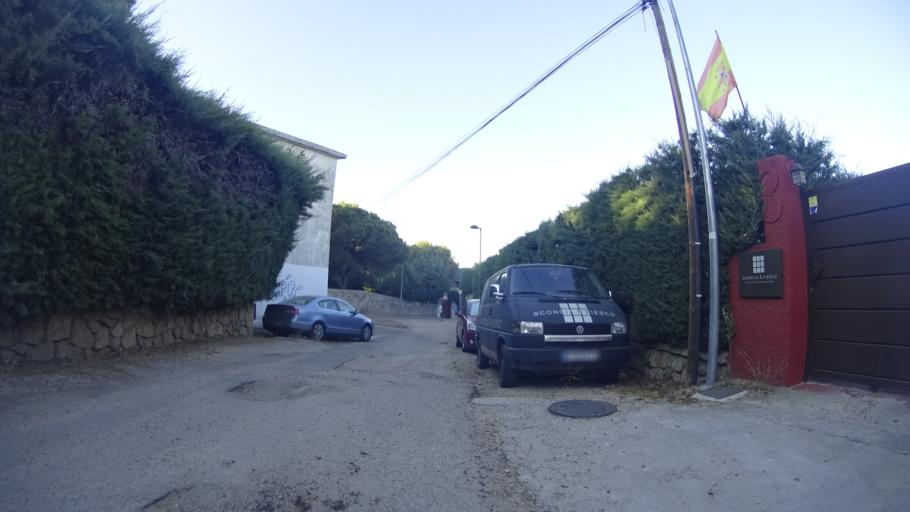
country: ES
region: Madrid
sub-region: Provincia de Madrid
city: Galapagar
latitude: 40.5661
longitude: -3.9995
